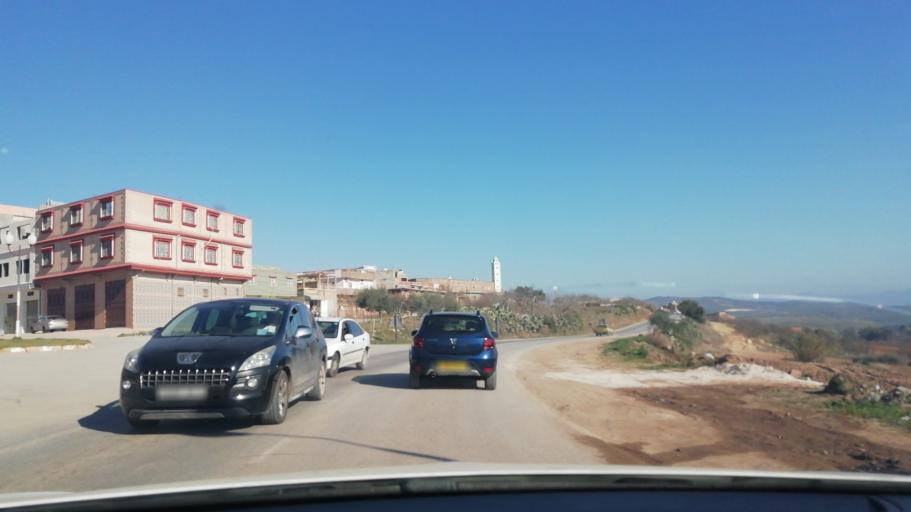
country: DZ
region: Tlemcen
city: Nedroma
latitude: 35.0042
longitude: -1.9036
